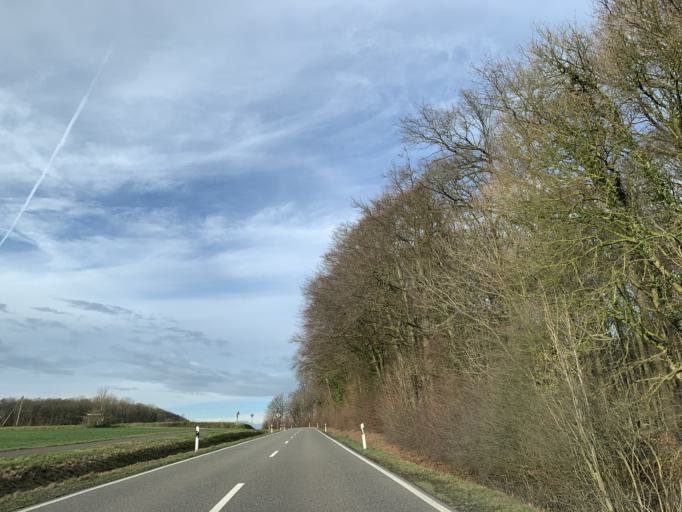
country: DE
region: North Rhine-Westphalia
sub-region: Regierungsbezirk Munster
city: Nottuln
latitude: 51.9456
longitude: 7.3293
